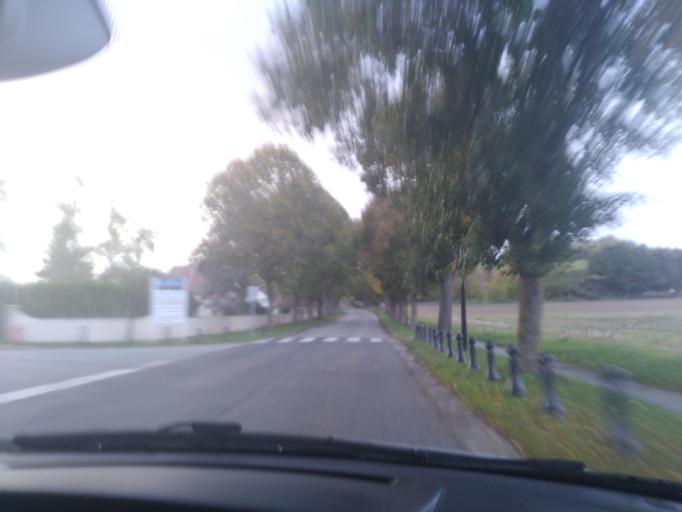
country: FR
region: Ile-de-France
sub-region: Departement des Yvelines
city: Chavenay
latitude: 48.8548
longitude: 1.9812
